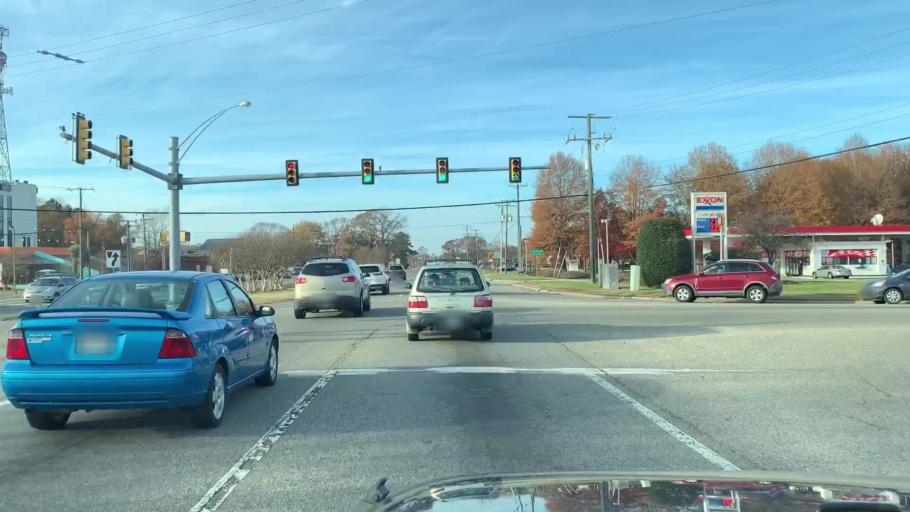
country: US
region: Virginia
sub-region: James City County
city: Williamsburg
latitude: 37.3401
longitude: -76.7543
